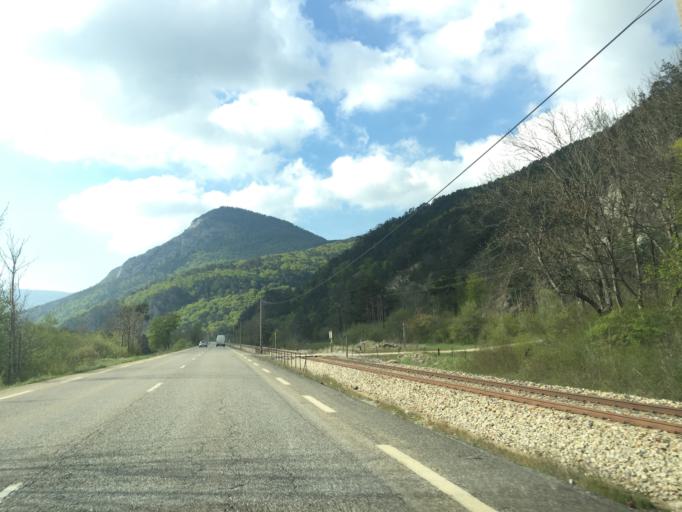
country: FR
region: Provence-Alpes-Cote d'Azur
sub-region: Departement des Hautes-Alpes
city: Veynes
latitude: 44.6035
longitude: 5.7086
